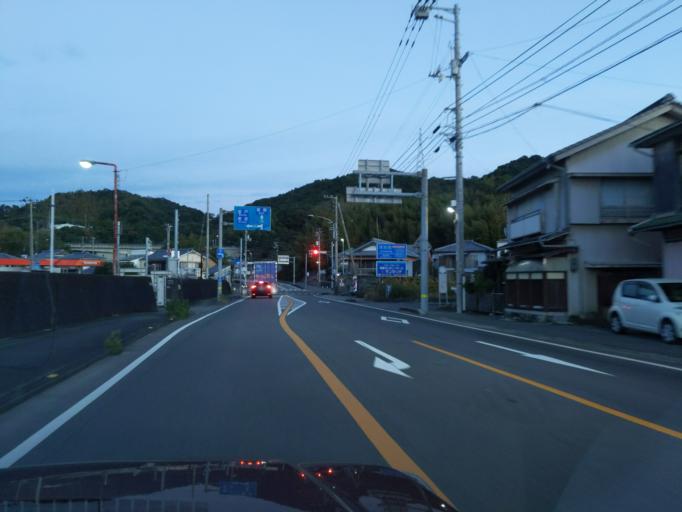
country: JP
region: Tokushima
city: Anan
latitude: 33.8725
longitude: 134.6379
